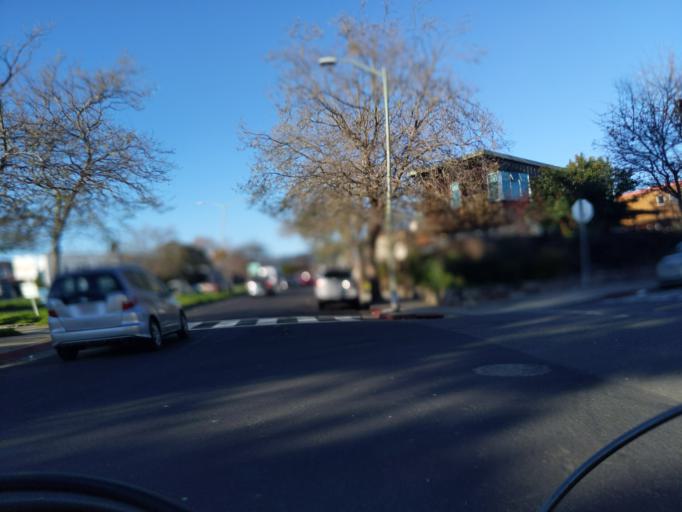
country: US
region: California
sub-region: Alameda County
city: Emeryville
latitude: 37.8458
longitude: -122.2727
